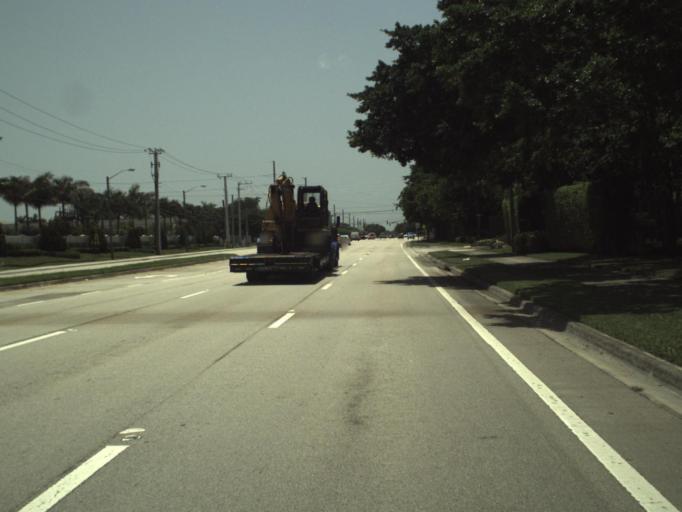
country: US
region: Florida
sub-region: Palm Beach County
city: Kings Point
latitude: 26.4114
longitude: -80.1465
